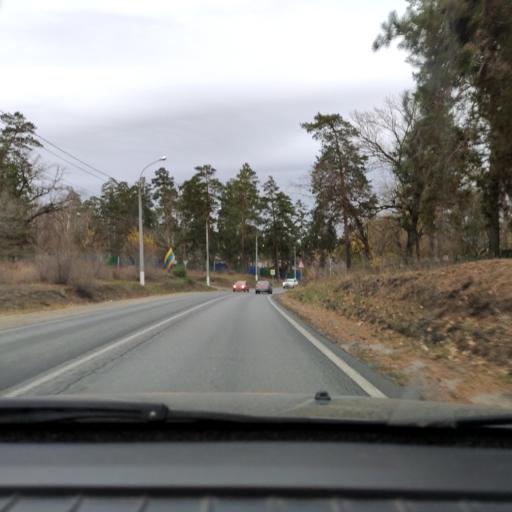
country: RU
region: Samara
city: Tol'yatti
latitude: 53.4816
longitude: 49.3213
